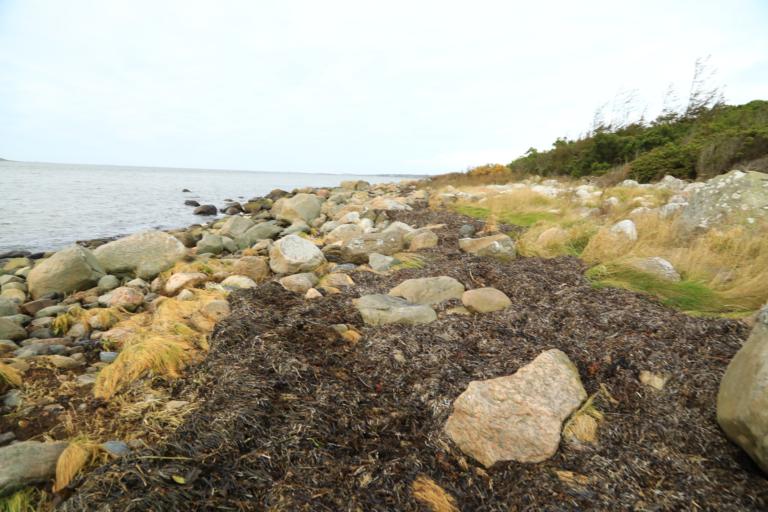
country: SE
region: Halland
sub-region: Varbergs Kommun
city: Varberg
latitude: 57.1705
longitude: 12.2053
